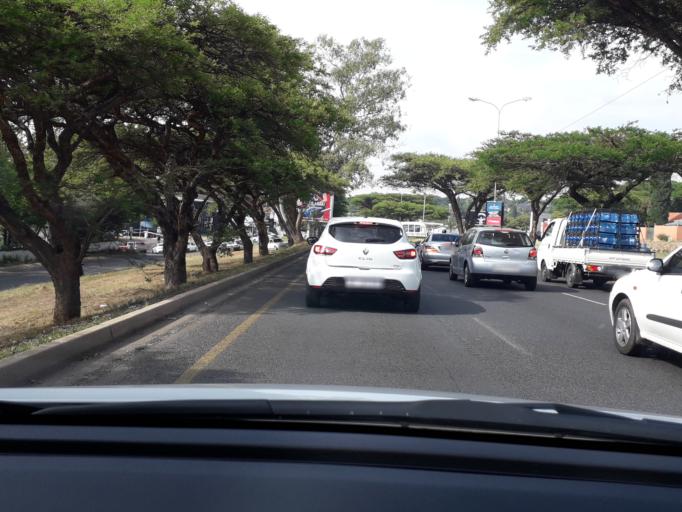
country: ZA
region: Gauteng
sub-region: City of Johannesburg Metropolitan Municipality
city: Johannesburg
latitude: -26.0791
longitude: 28.0257
